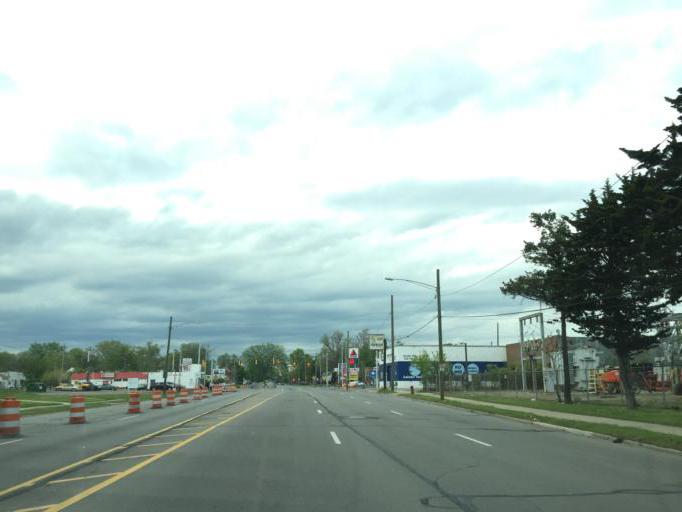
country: US
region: Michigan
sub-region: Wayne County
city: Redford
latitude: 42.3848
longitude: -83.2368
